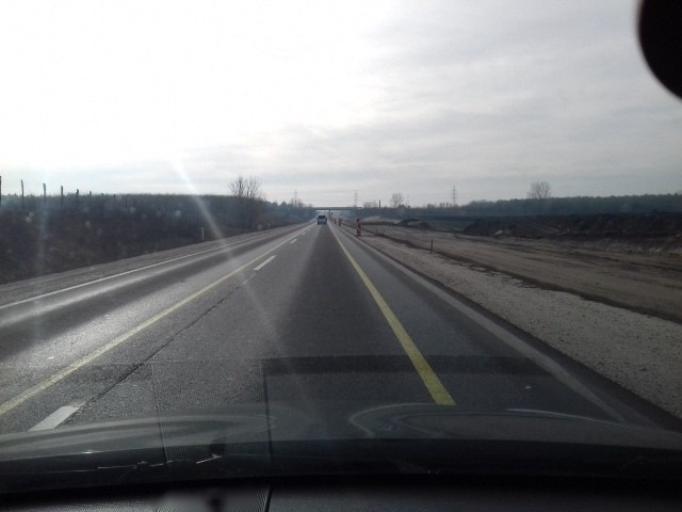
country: HU
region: Pest
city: God
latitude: 47.6713
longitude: 19.1681
